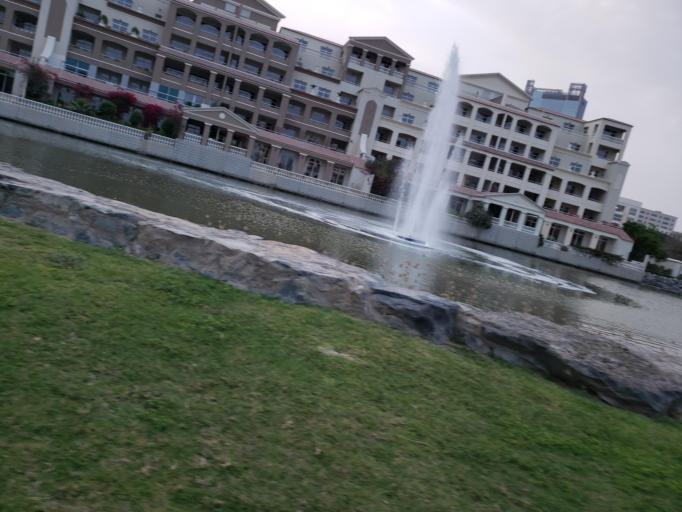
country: AE
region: Dubai
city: Dubai
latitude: 25.0416
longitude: 55.2323
